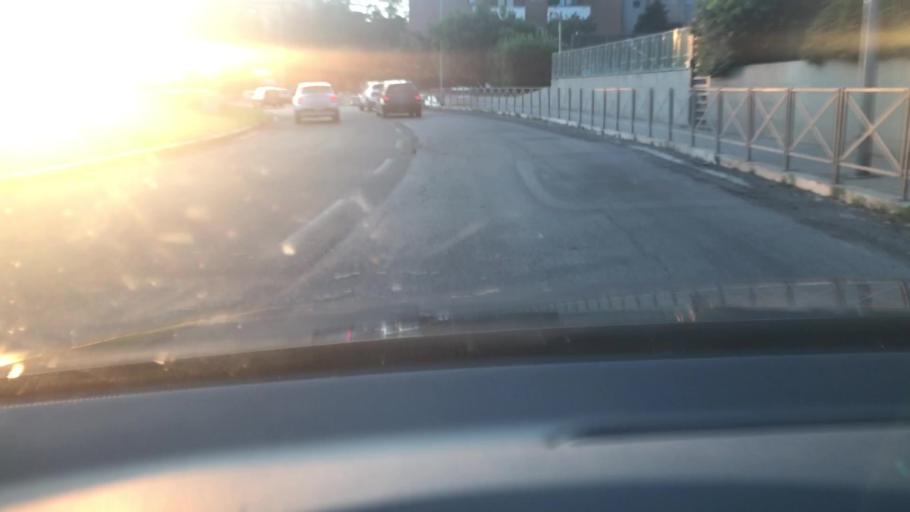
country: IT
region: Latium
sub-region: Citta metropolitana di Roma Capitale
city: Rome
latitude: 41.9312
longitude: 12.5613
